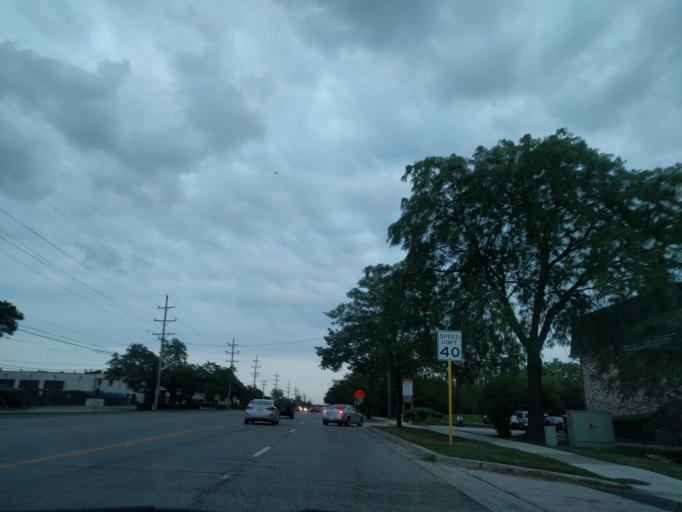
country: US
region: Illinois
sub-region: Cook County
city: Elk Grove Village
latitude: 42.0321
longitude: -87.9601
